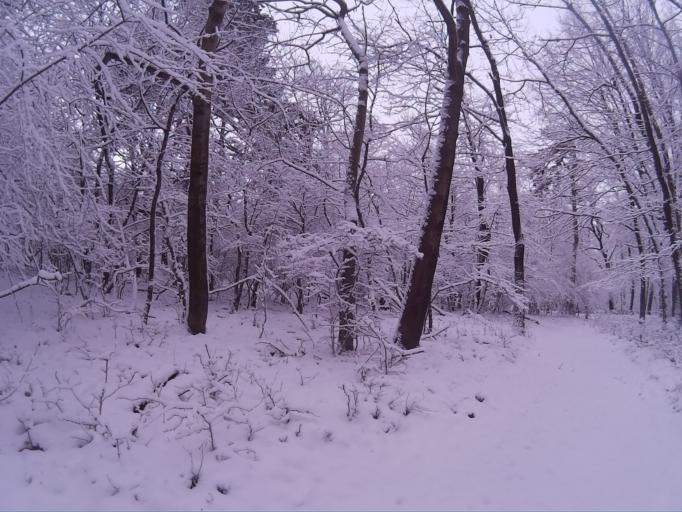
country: HU
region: Komarom-Esztergom
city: Tarjan
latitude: 47.5728
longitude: 18.5365
